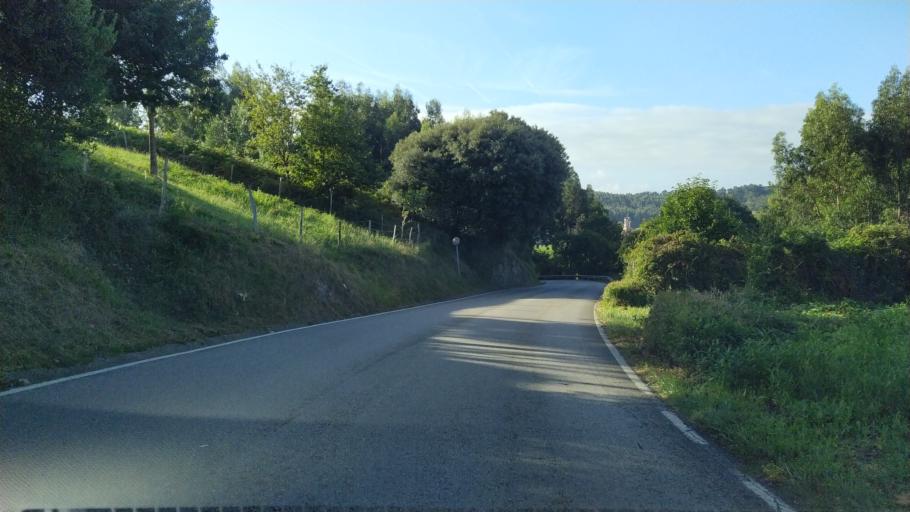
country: ES
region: Cantabria
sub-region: Provincia de Cantabria
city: Santa Cruz de Bezana
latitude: 43.4512
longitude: -3.9282
